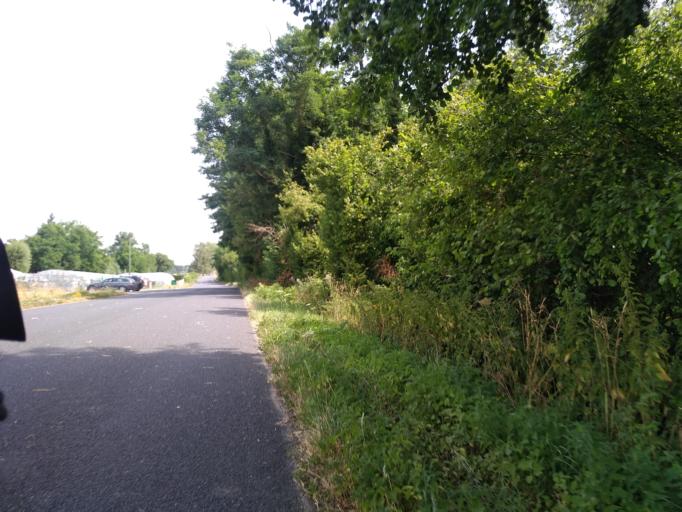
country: FR
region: Auvergne
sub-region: Departement de l'Allier
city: Molinet
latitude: 46.4619
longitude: 3.9644
